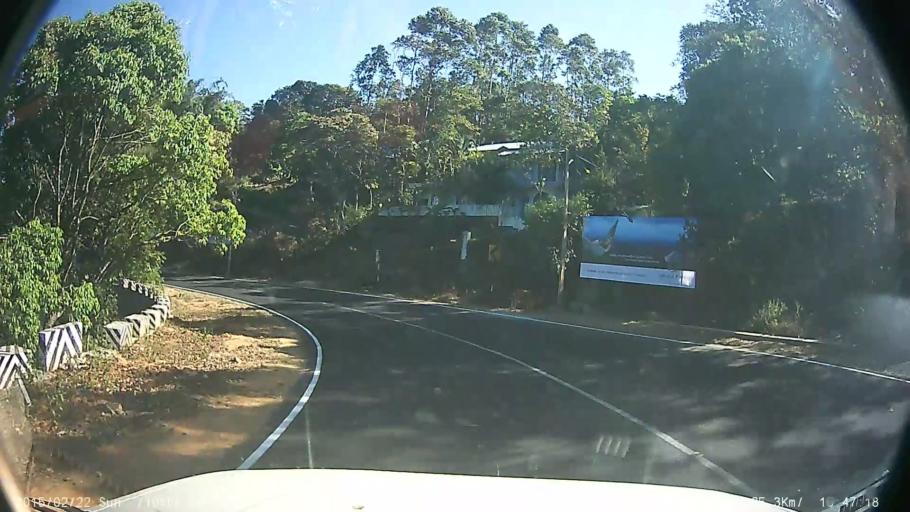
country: IN
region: Kerala
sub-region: Kottayam
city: Erattupetta
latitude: 9.5779
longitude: 76.9895
